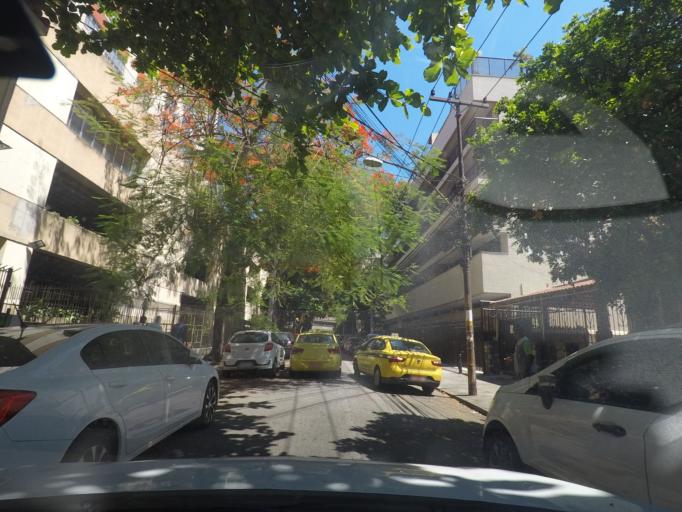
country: BR
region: Rio de Janeiro
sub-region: Rio De Janeiro
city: Rio de Janeiro
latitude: -22.9204
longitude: -43.2364
